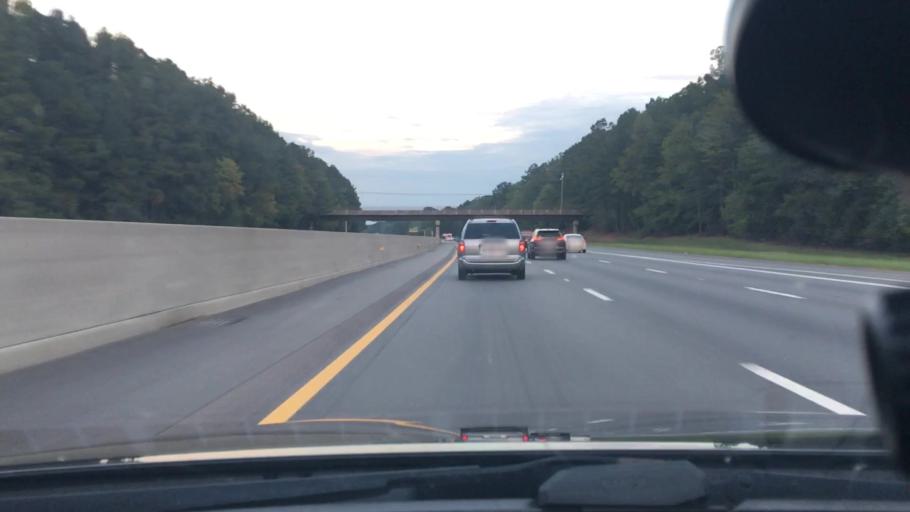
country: US
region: North Carolina
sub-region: Wake County
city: West Raleigh
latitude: 35.7517
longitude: -78.6970
